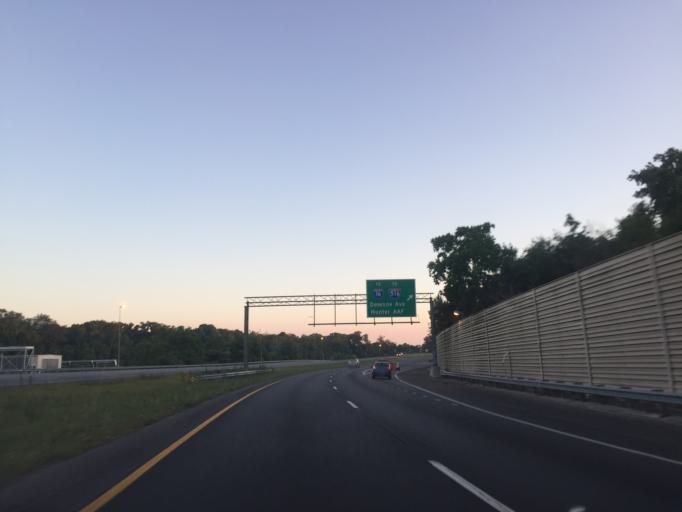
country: US
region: Georgia
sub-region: Chatham County
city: Thunderbolt
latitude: 32.0183
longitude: -81.0876
